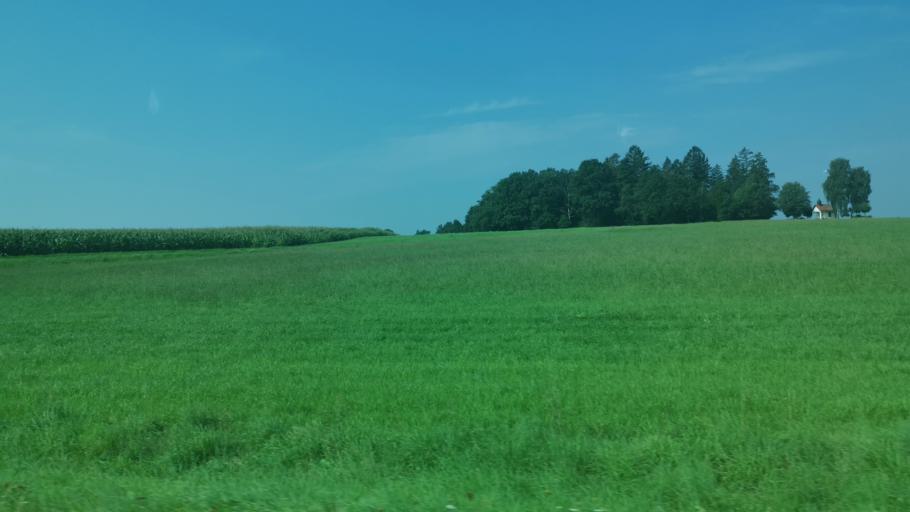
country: DE
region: Bavaria
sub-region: Upper Palatinate
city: Pemfling
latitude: 49.2670
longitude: 12.6310
